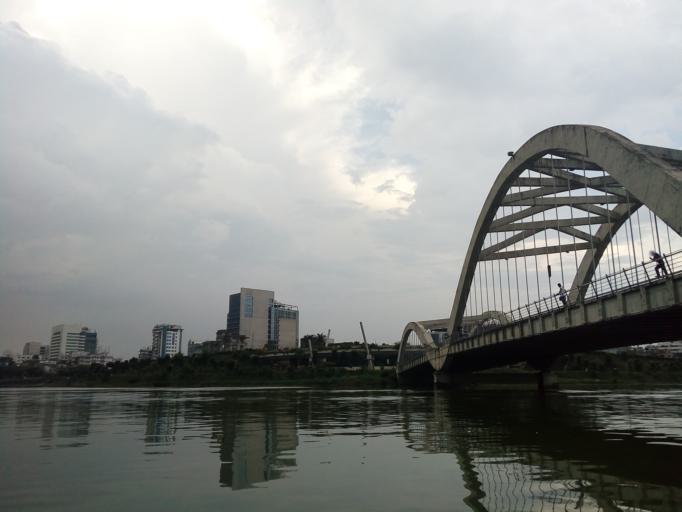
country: BD
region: Dhaka
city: Paltan
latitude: 23.7674
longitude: 90.4132
